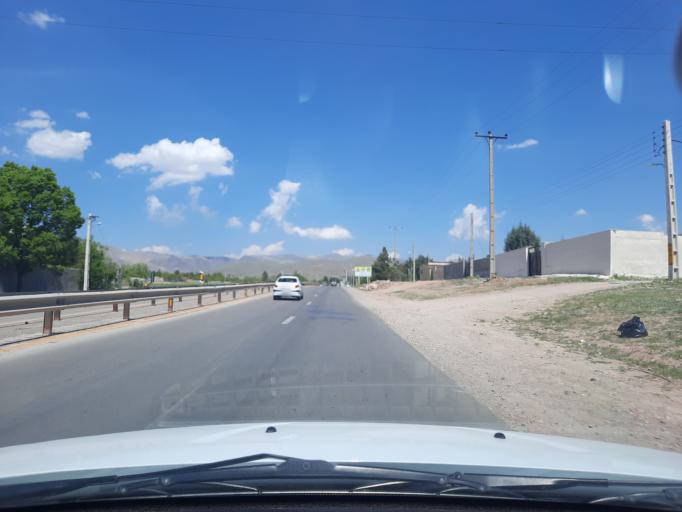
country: IR
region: Qazvin
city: Alvand
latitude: 36.2980
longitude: 50.1402
